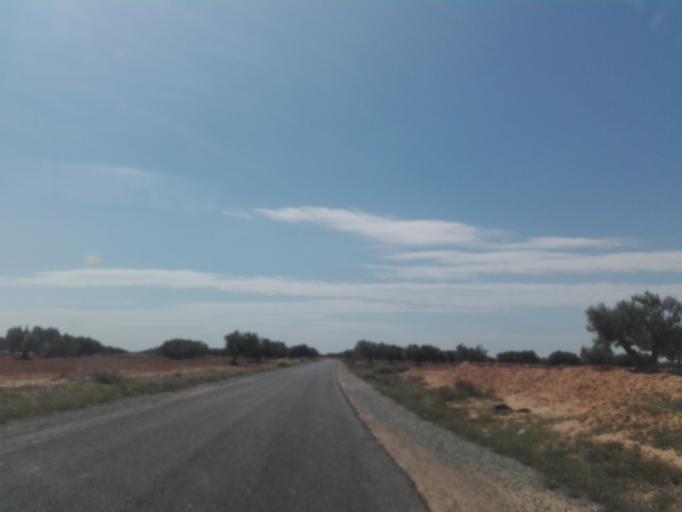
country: TN
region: Safaqis
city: Sfax
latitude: 34.6789
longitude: 10.5699
